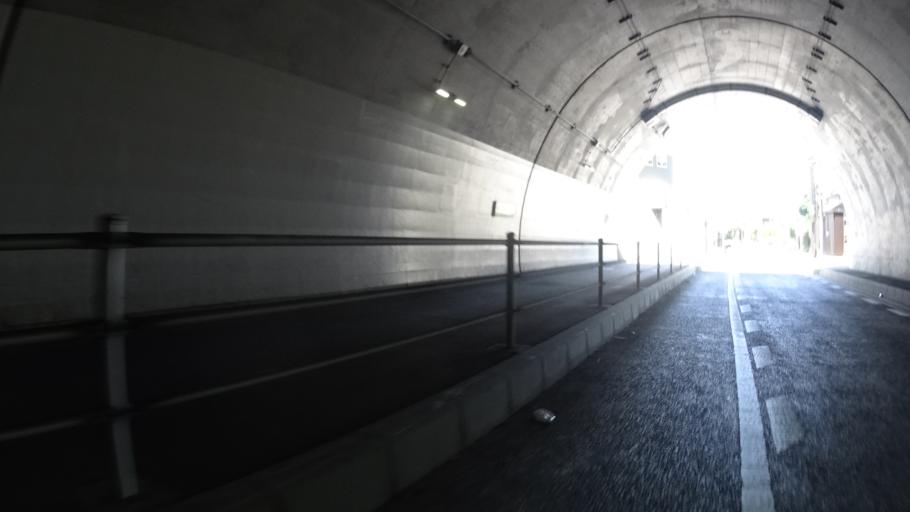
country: JP
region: Kanagawa
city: Zushi
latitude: 35.2888
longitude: 139.5801
